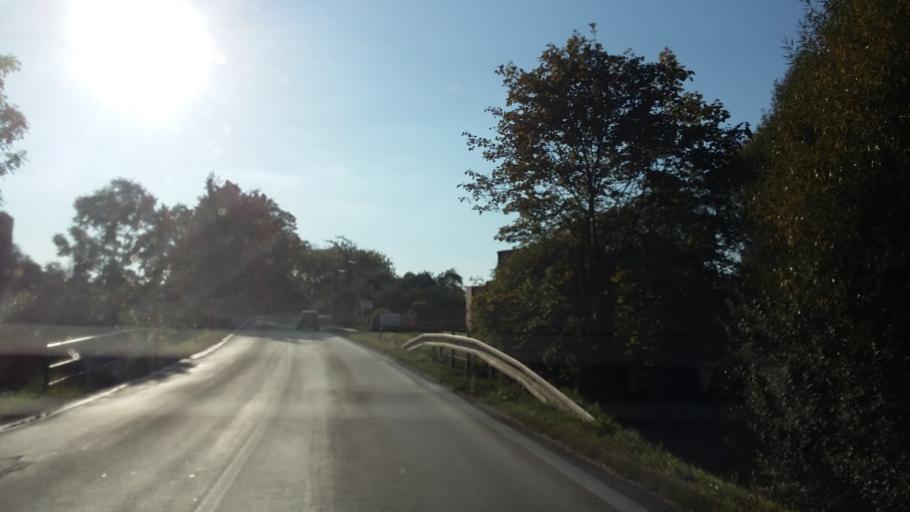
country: CZ
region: Vysocina
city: Merin
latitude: 49.3788
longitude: 15.9338
